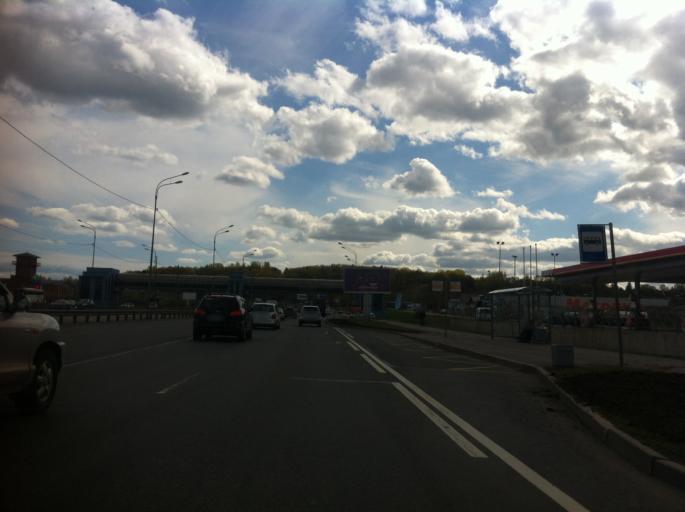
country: RU
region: St.-Petersburg
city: Aleksandrovskaya
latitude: 59.7823
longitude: 30.3249
